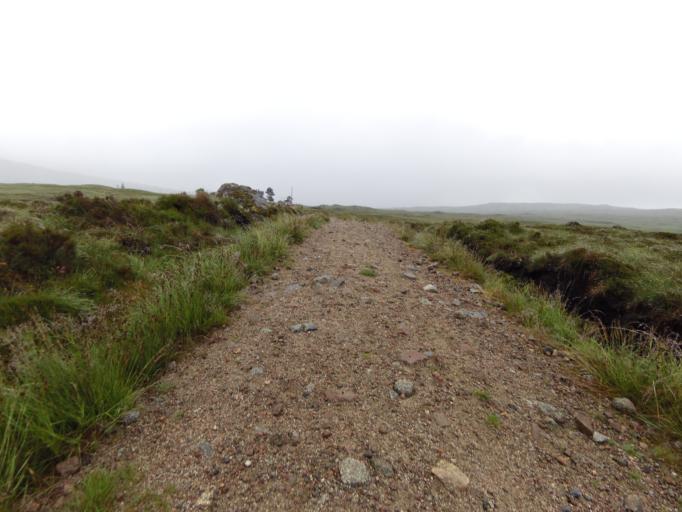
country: GB
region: Scotland
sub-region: Highland
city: Spean Bridge
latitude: 56.7618
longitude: -4.6940
